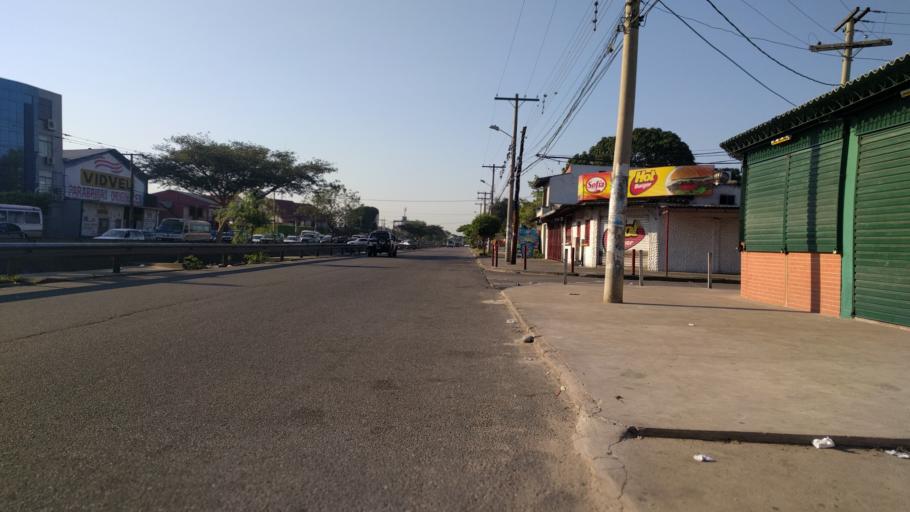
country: BO
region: Santa Cruz
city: Santa Cruz de la Sierra
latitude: -17.8001
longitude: -63.1684
